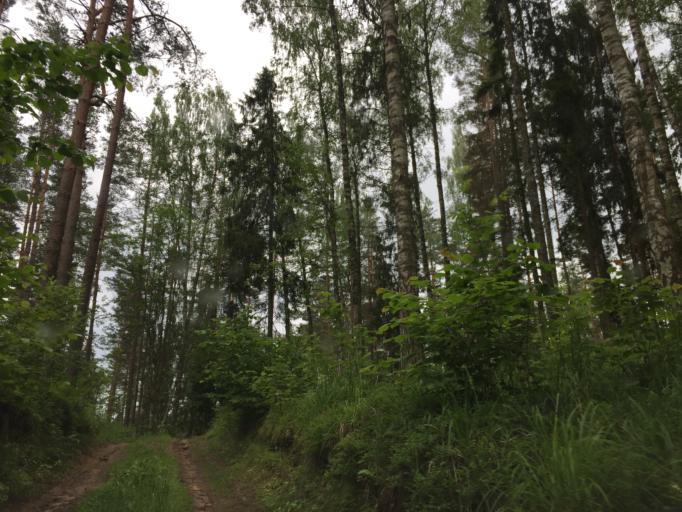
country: LV
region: Tukuma Rajons
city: Tukums
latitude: 57.0289
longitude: 23.0771
